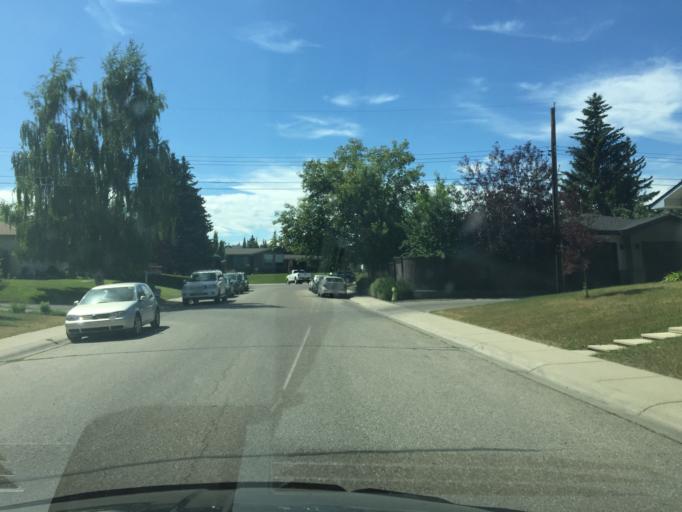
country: CA
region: Alberta
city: Calgary
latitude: 50.9464
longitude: -114.0548
